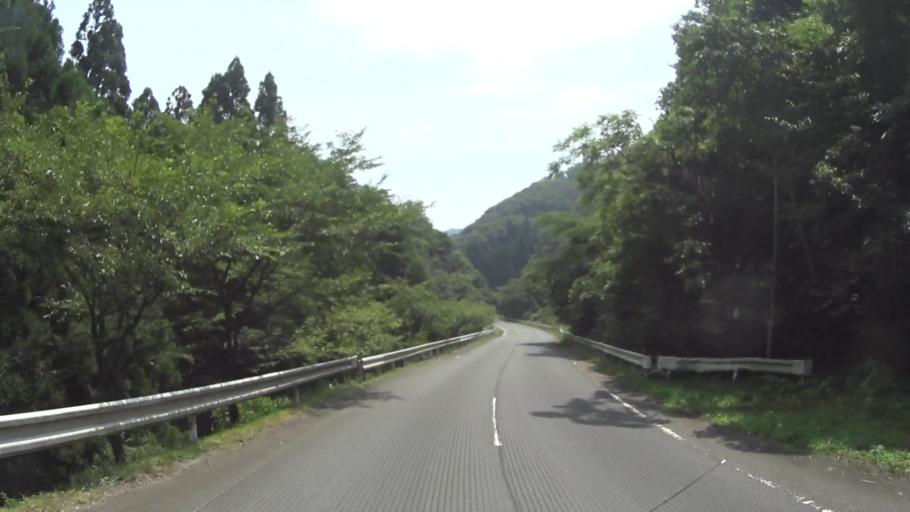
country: JP
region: Kyoto
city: Ayabe
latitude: 35.2019
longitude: 135.3744
